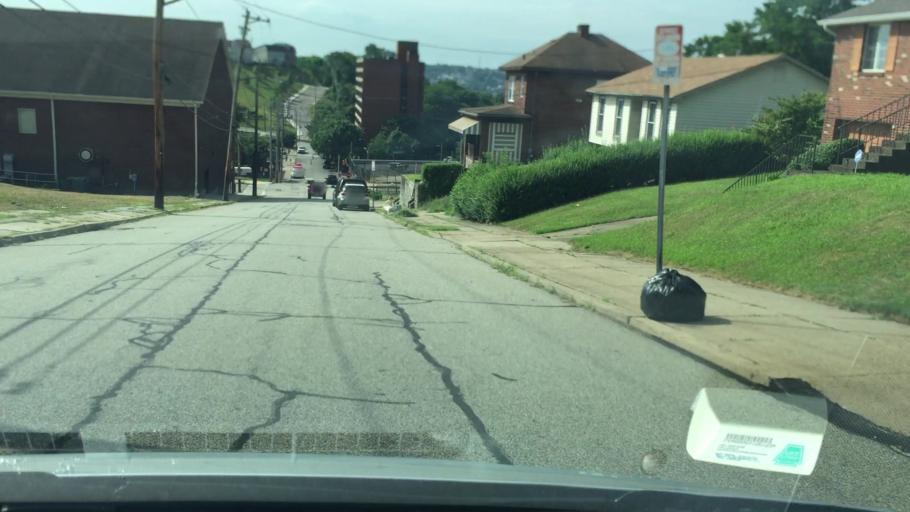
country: US
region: Pennsylvania
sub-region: Allegheny County
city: Pittsburgh
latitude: 40.4452
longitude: -79.9815
